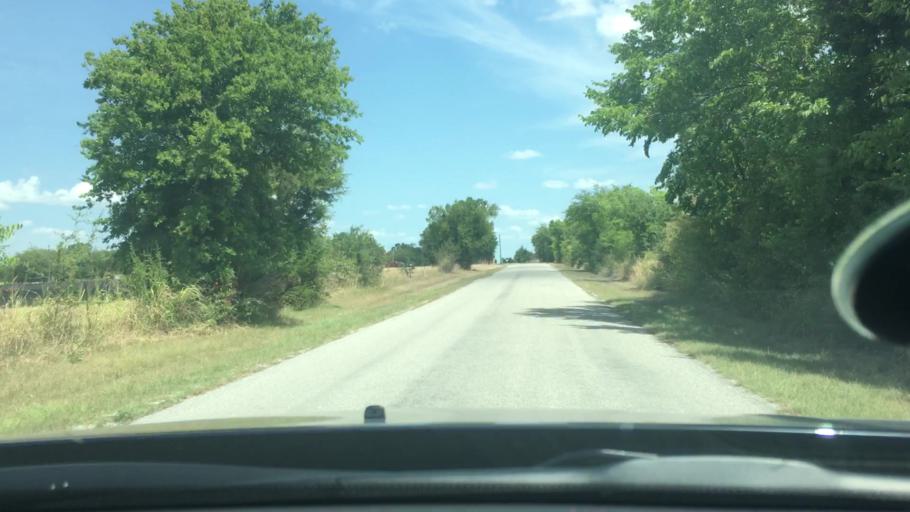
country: US
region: Oklahoma
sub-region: Love County
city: Marietta
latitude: 34.0074
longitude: -97.1934
